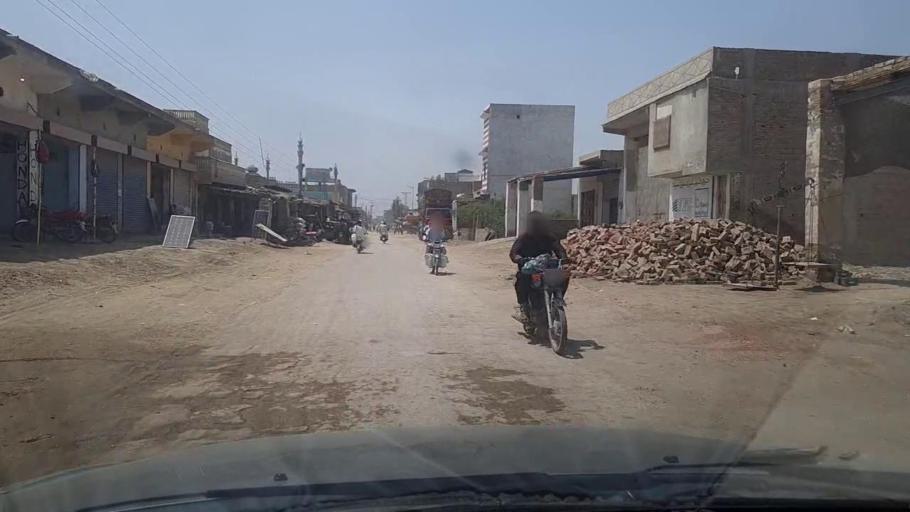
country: PK
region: Sindh
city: Bhiria
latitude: 26.8846
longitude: 68.2887
